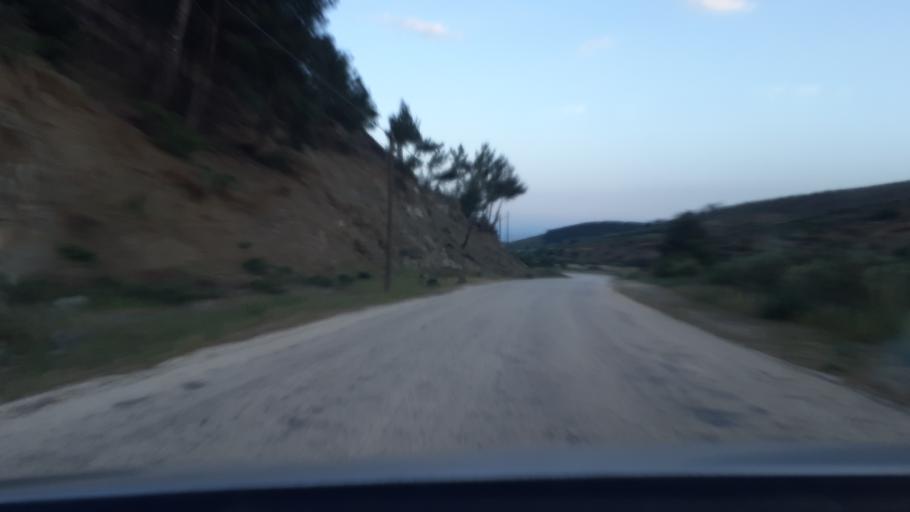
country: TR
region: Hatay
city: Kirikhan
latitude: 36.5152
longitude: 36.3192
